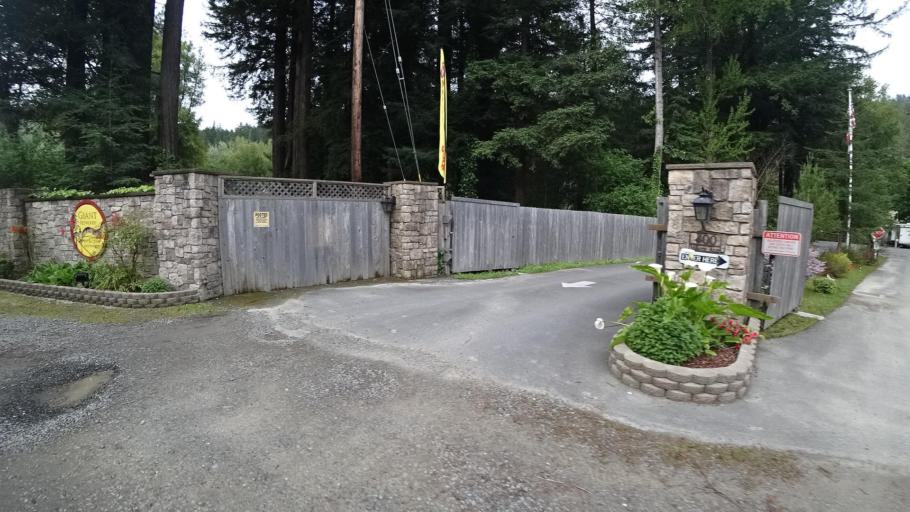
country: US
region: California
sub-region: Humboldt County
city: Redway
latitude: 40.2624
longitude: -123.8776
